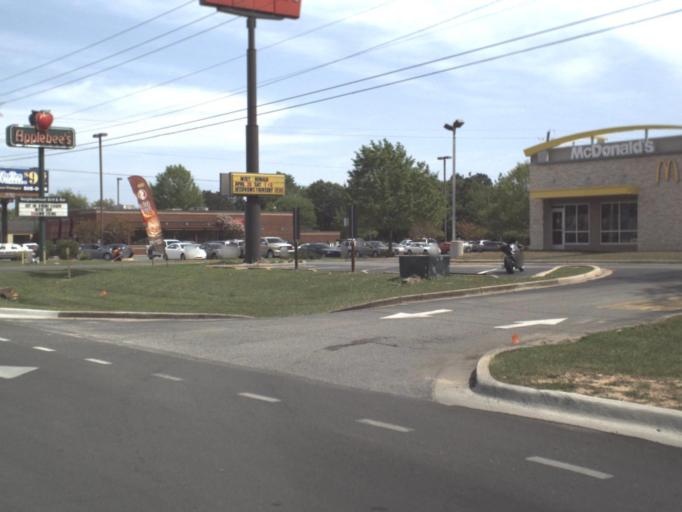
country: US
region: Florida
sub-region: Escambia County
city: Ensley
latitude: 30.5330
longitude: -87.2672
